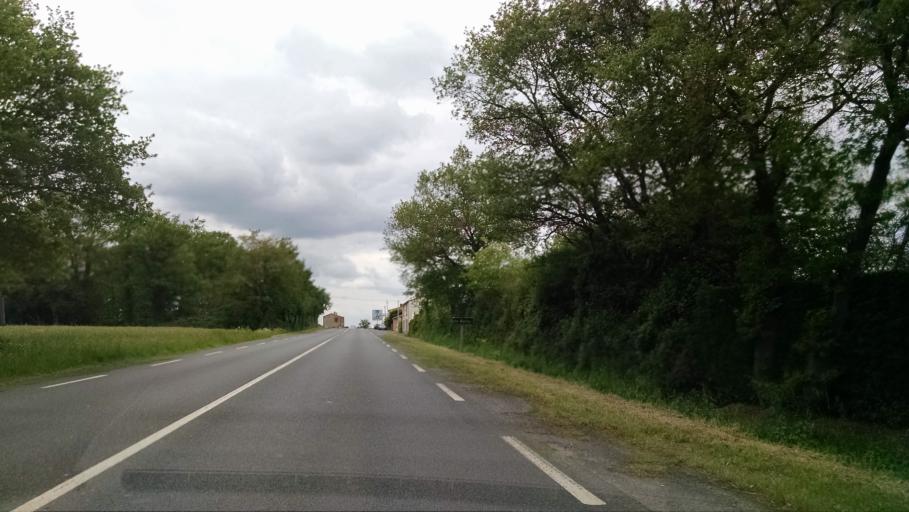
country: FR
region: Pays de la Loire
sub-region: Departement de la Loire-Atlantique
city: Aigrefeuille-sur-Maine
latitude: 47.0943
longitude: -1.4440
